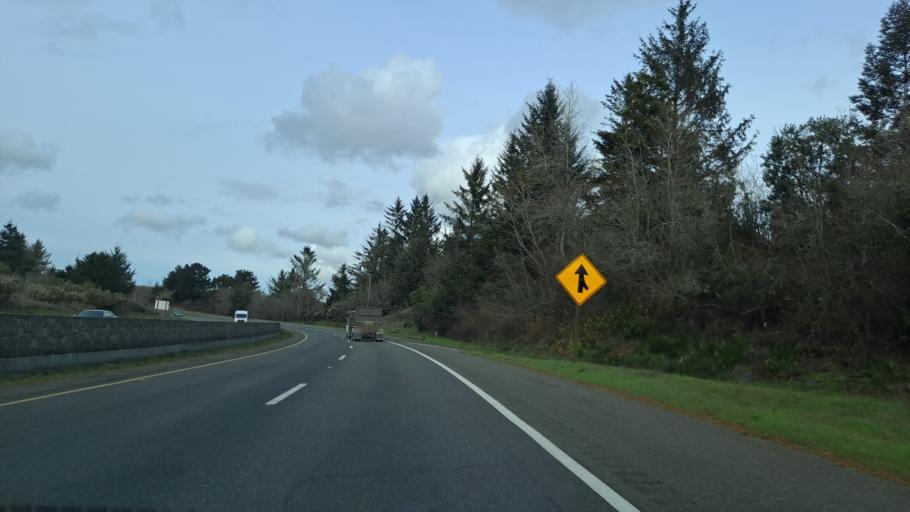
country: US
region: California
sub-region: Humboldt County
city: Fortuna
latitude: 40.6432
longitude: -124.2085
